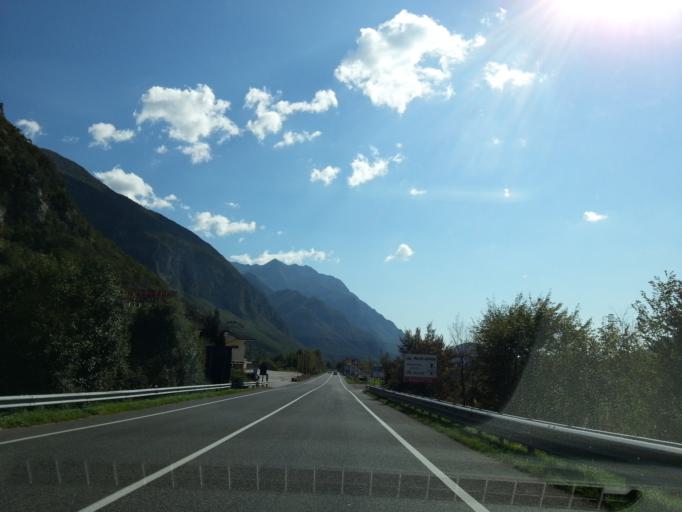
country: IT
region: Friuli Venezia Giulia
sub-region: Provincia di Udine
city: Venzone
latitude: 46.3652
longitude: 13.1348
